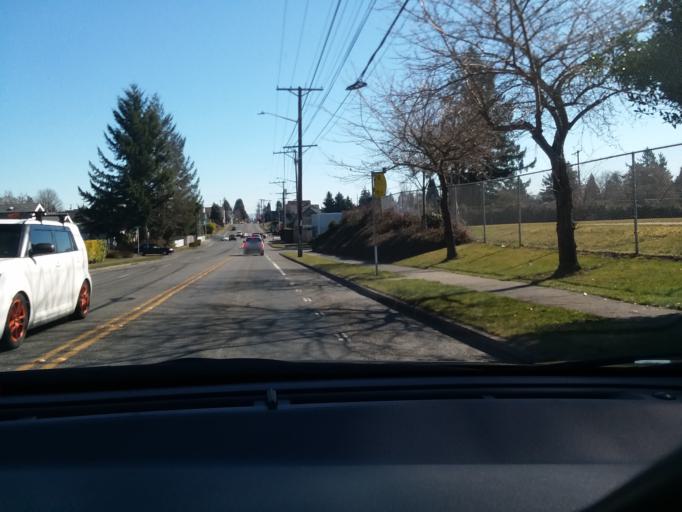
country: US
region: Washington
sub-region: Pierce County
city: Tacoma
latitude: 47.2500
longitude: -122.4787
